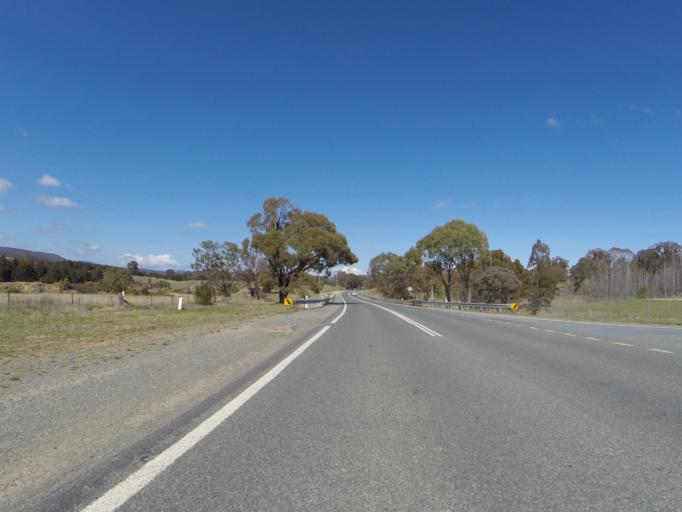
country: AU
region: New South Wales
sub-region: Queanbeyan
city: Queanbeyan
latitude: -35.3229
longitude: 149.2407
